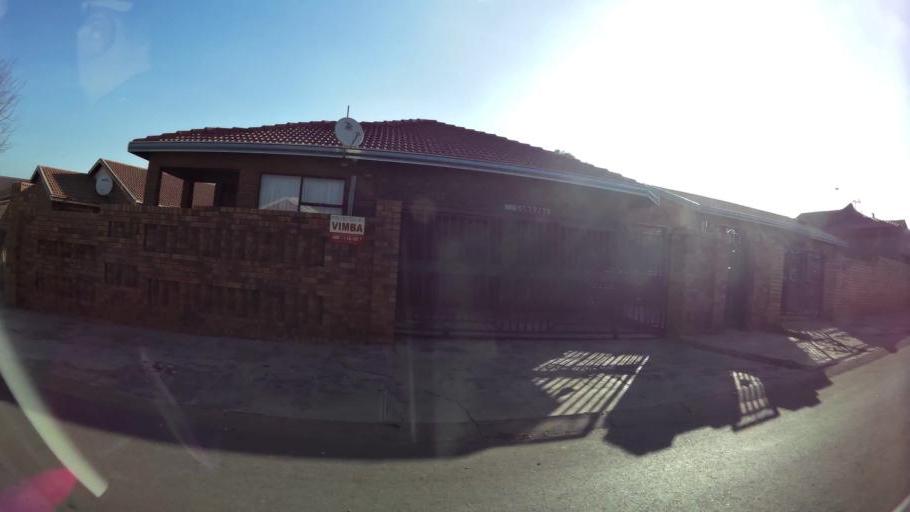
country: ZA
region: Gauteng
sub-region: City of Johannesburg Metropolitan Municipality
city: Soweto
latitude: -26.2736
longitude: 27.9154
